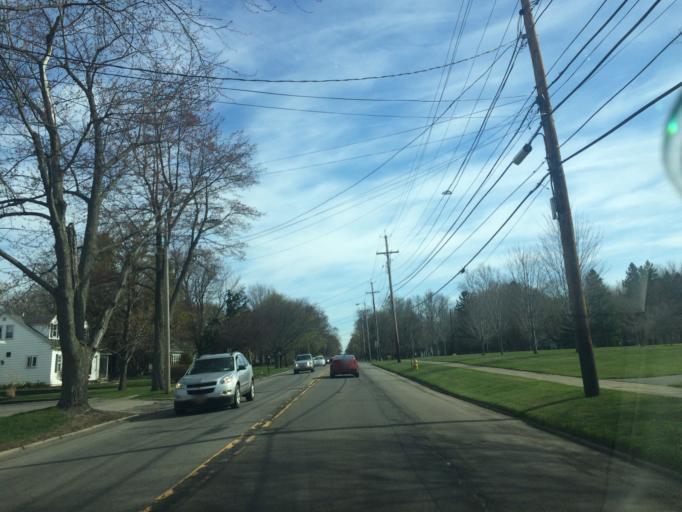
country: US
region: New York
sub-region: Monroe County
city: Webster
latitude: 43.2082
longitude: -77.4303
